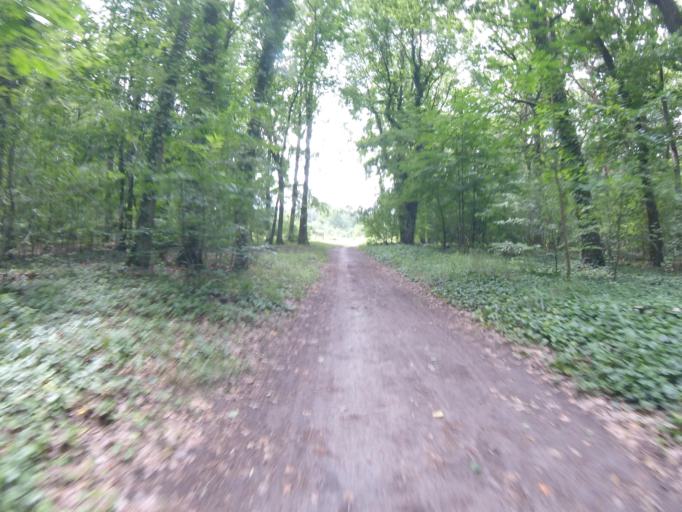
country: DE
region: Brandenburg
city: Konigs Wusterhausen
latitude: 52.2893
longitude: 13.6412
